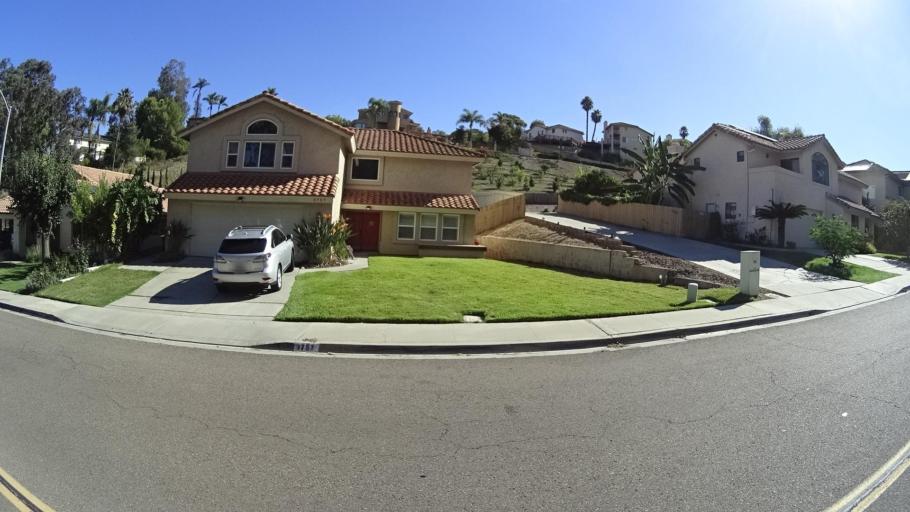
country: US
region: California
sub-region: San Diego County
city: Bonita
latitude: 32.6672
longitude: -117.0165
